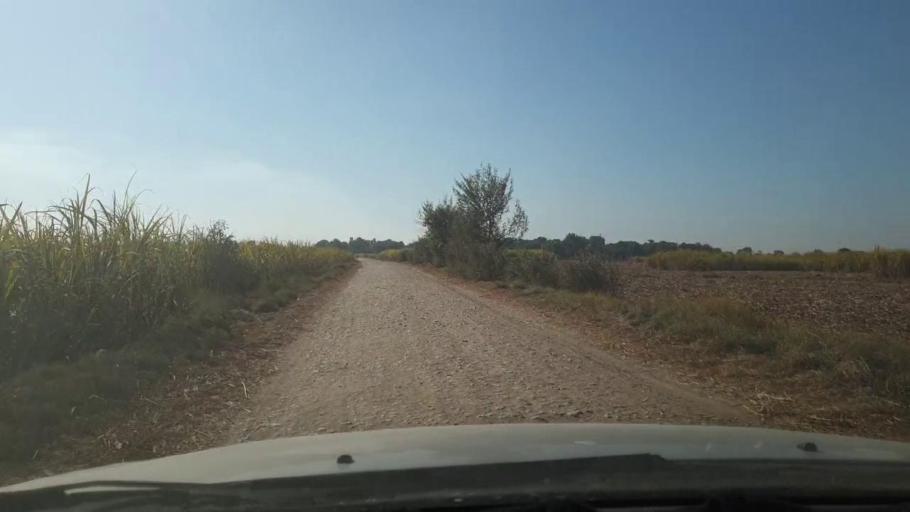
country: PK
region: Sindh
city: Ghotki
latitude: 27.9772
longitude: 69.1923
